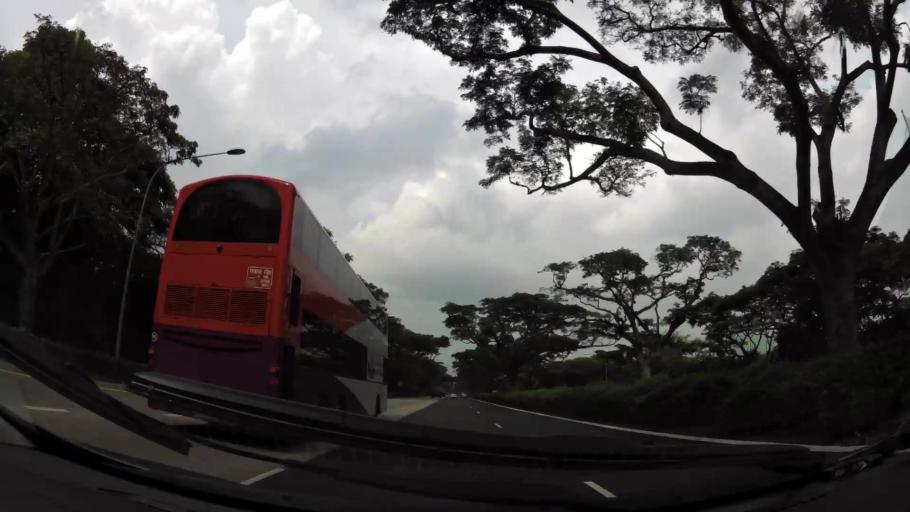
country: SG
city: Singapore
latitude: 1.3283
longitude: 103.9741
